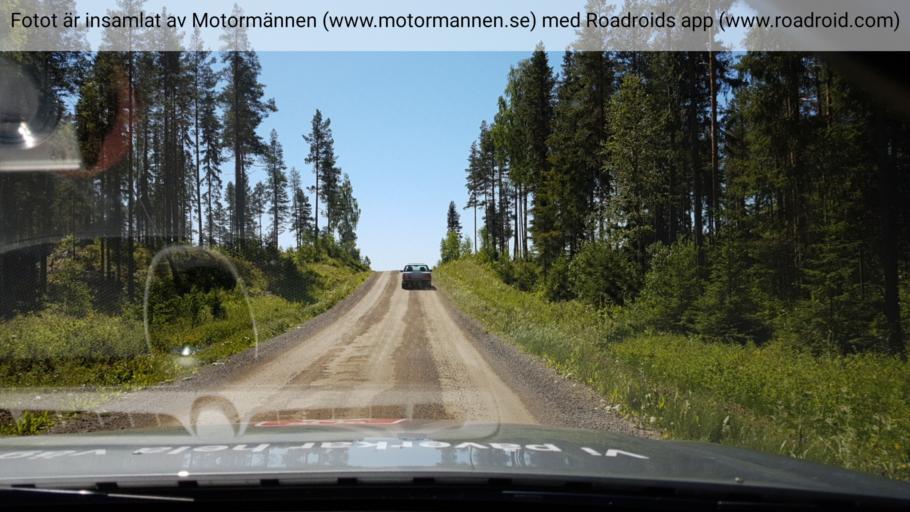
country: SE
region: Jaemtland
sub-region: Braecke Kommun
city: Braecke
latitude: 62.8214
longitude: 15.2218
